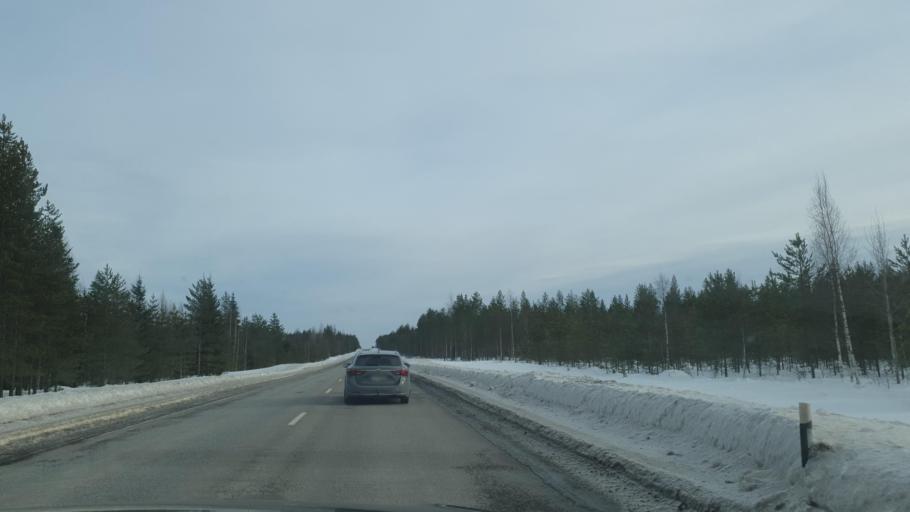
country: FI
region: Kainuu
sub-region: Kajaani
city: Vaala
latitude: 64.5536
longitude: 27.0487
